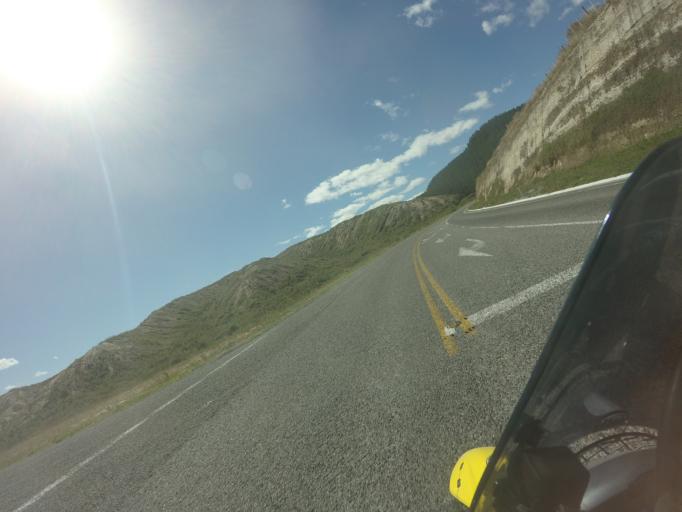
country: NZ
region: Bay of Plenty
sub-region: Whakatane District
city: Murupara
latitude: -38.3154
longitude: 176.8003
